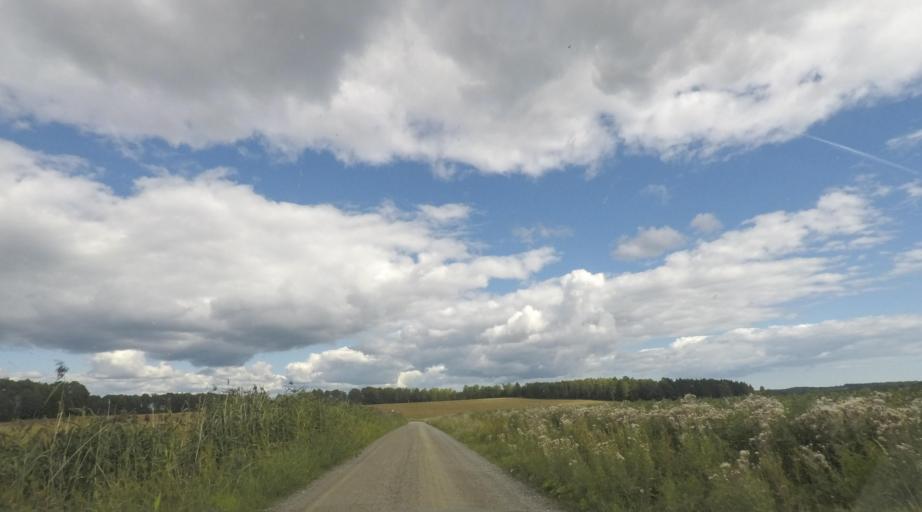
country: SE
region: Stockholm
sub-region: Sodertalje Kommun
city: Pershagen
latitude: 59.1131
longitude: 17.6623
